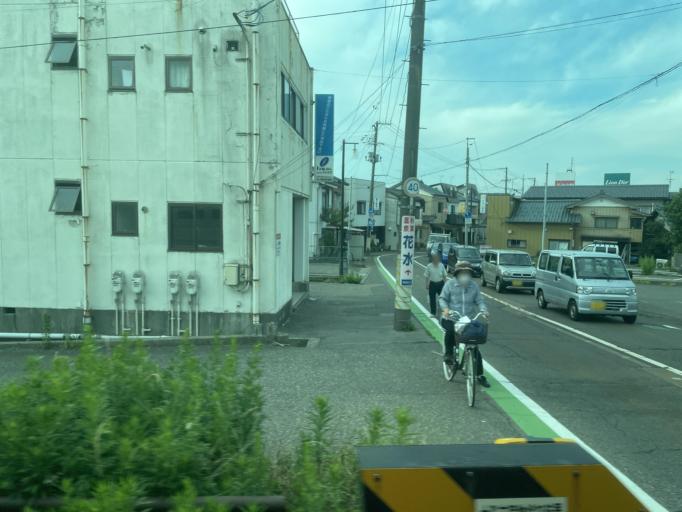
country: JP
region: Niigata
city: Niitsu-honcho
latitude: 37.7925
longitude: 139.1260
